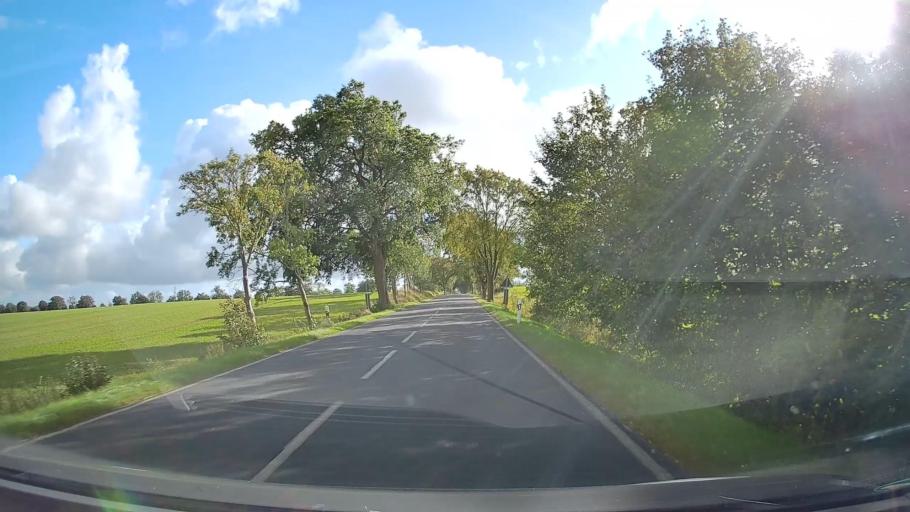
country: DE
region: Mecklenburg-Vorpommern
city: Putbus
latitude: 54.3720
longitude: 13.4798
